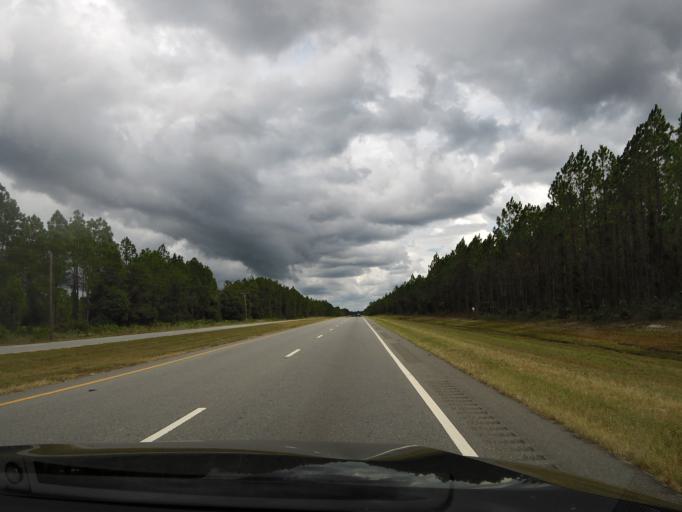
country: US
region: Georgia
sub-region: Brantley County
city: Nahunta
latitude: 31.2106
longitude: -81.9356
